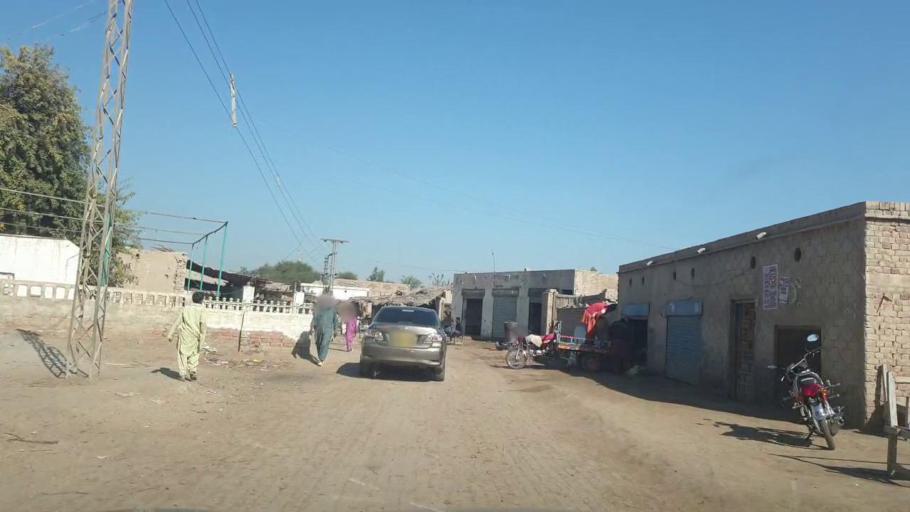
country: PK
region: Sindh
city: Mirpur Mathelo
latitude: 28.1421
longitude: 69.5337
